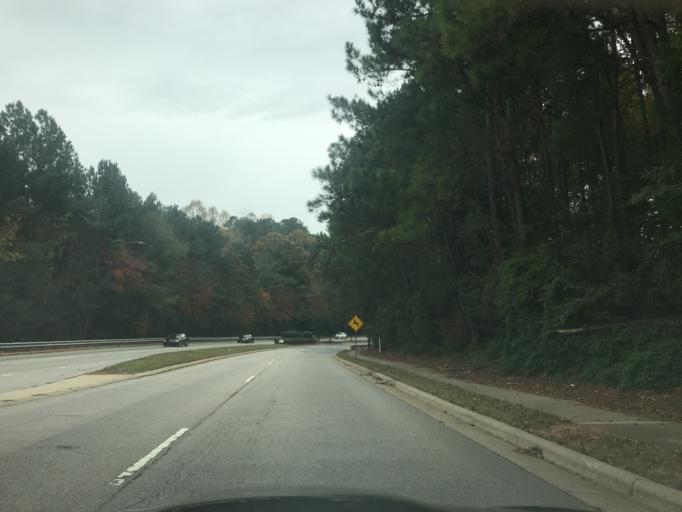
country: US
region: North Carolina
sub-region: Wake County
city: West Raleigh
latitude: 35.8560
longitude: -78.6577
